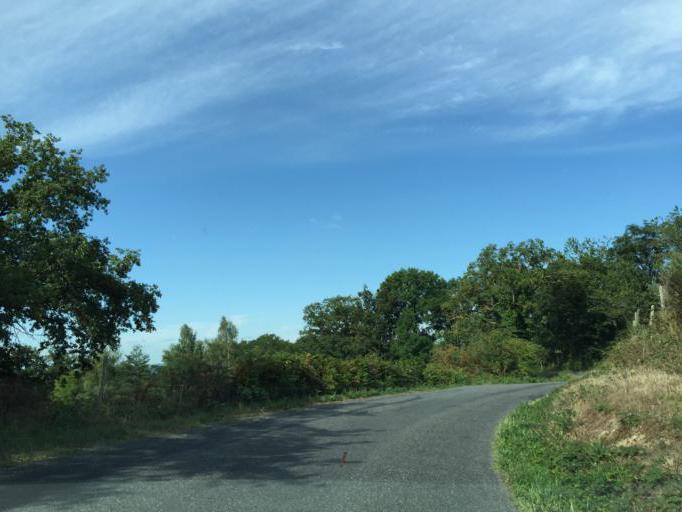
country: FR
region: Midi-Pyrenees
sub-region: Departement de l'Aveyron
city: Sainte-Radegonde
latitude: 44.3164
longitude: 2.6689
